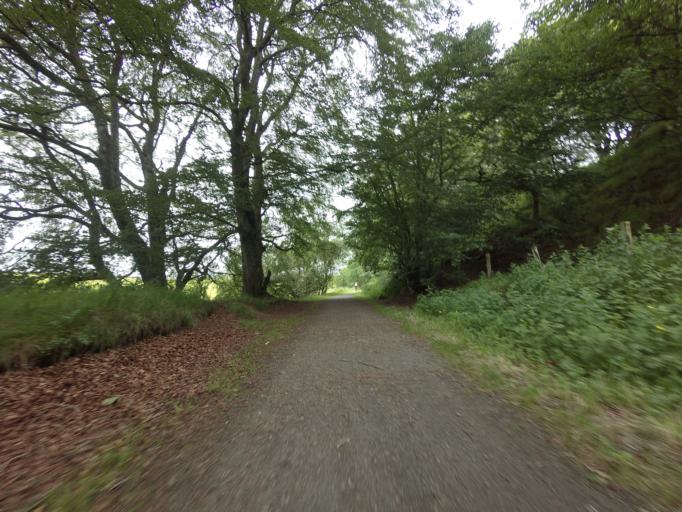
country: GB
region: Scotland
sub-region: Aberdeenshire
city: Mintlaw
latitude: 57.5101
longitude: -2.1415
